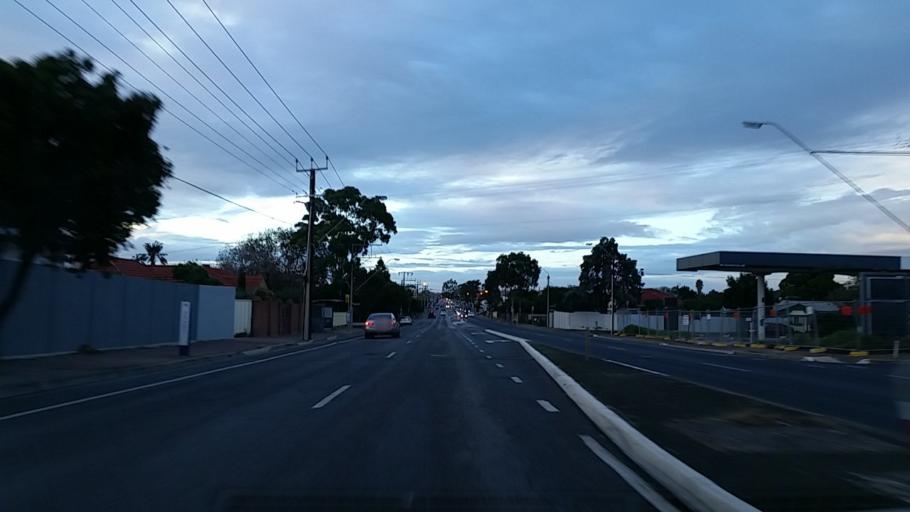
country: AU
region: South Australia
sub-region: Adelaide Hills
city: Seacliff
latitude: -35.0268
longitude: 138.5237
